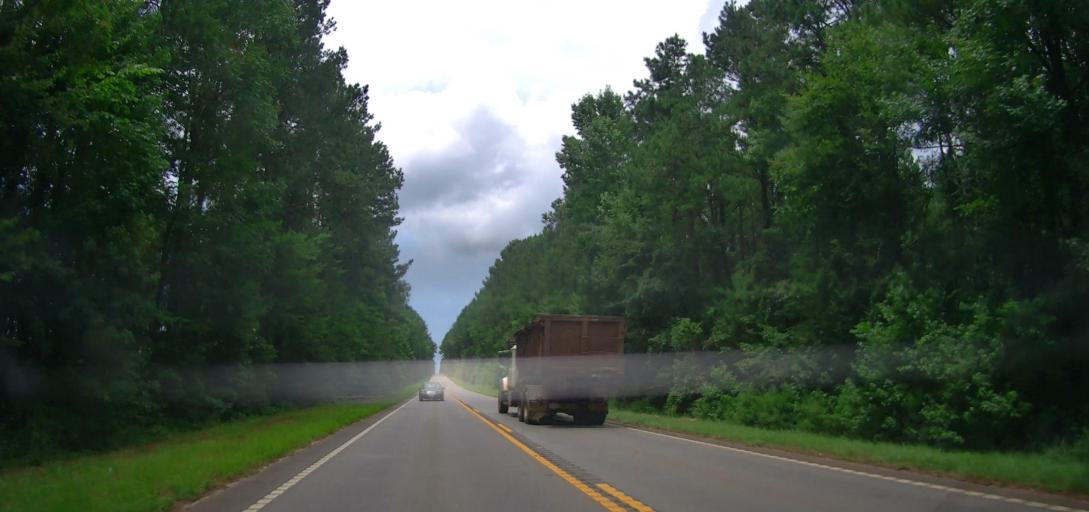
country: US
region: Georgia
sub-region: Pulaski County
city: Hawkinsville
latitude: 32.3819
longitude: -83.5513
